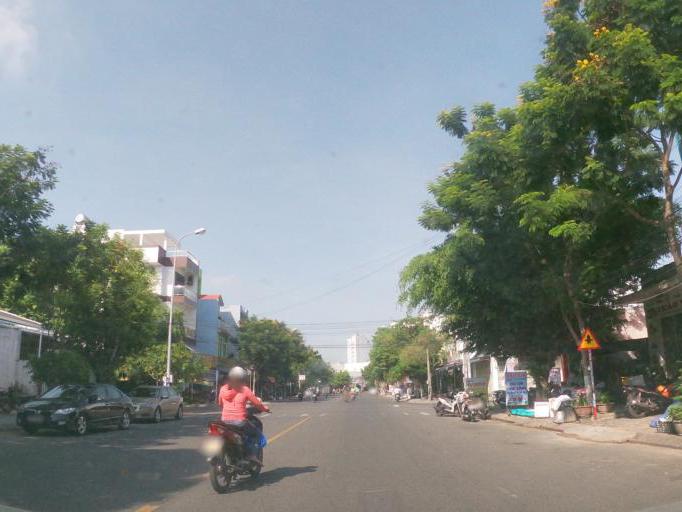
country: VN
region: Da Nang
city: Da Nang
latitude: 16.0822
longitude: 108.2321
